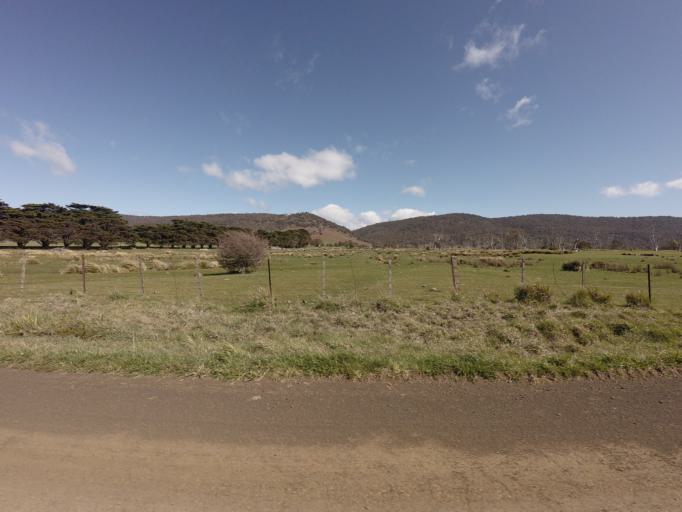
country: AU
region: Tasmania
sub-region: Northern Midlands
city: Evandale
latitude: -41.9494
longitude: 147.4343
